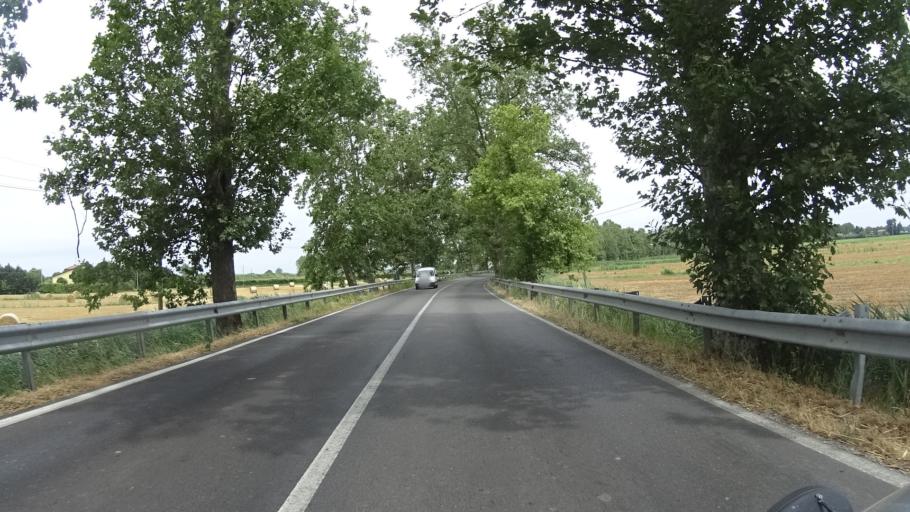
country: IT
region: Veneto
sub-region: Provincia di Venezia
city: La Salute di Livenza
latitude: 45.6931
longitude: 12.8449
